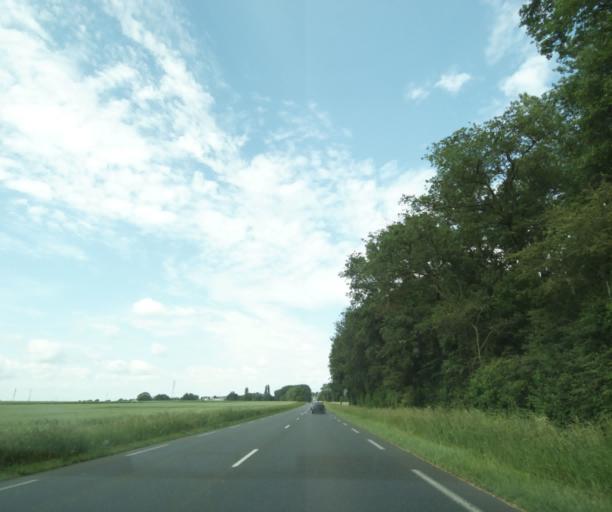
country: FR
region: Pays de la Loire
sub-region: Departement de Maine-et-Loire
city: Distre
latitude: 47.1857
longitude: -0.1307
